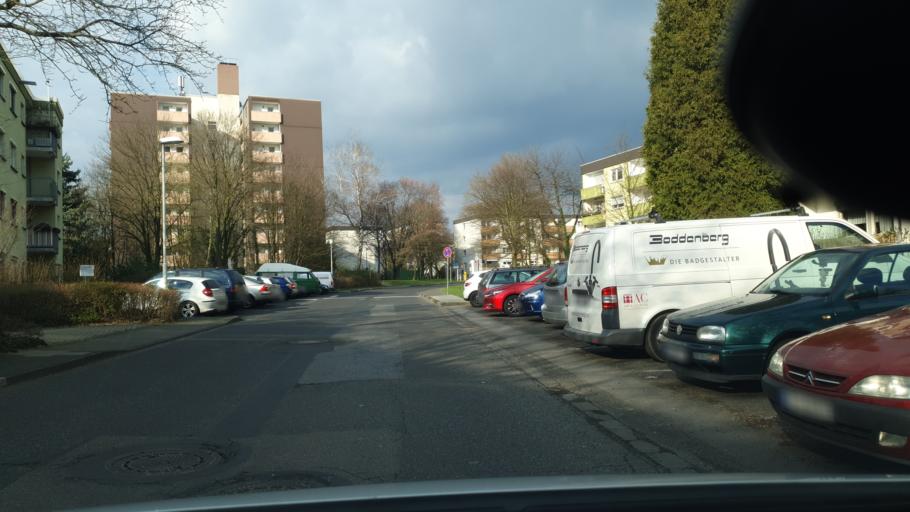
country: DE
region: North Rhine-Westphalia
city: Opladen
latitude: 51.0480
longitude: 7.0550
